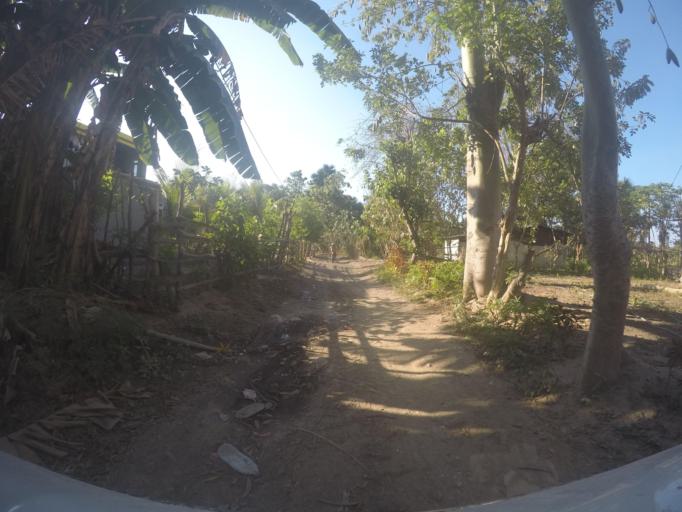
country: ID
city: Metinaro
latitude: -8.5435
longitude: 125.6656
